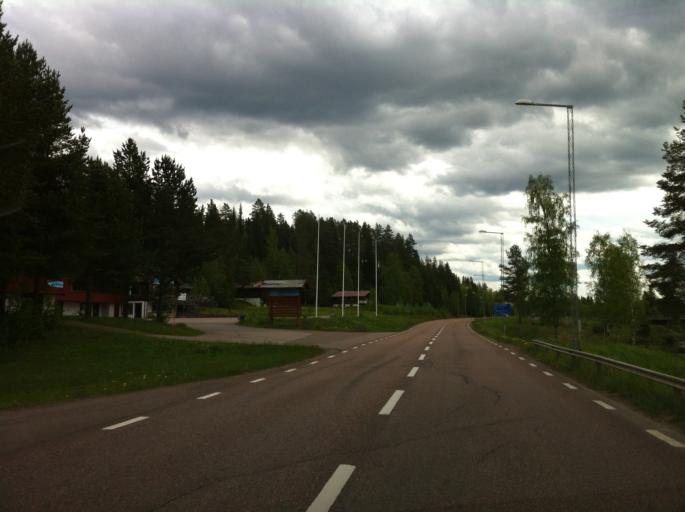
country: SE
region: Dalarna
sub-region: Malung-Saelens kommun
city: Malung
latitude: 61.1892
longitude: 13.2422
